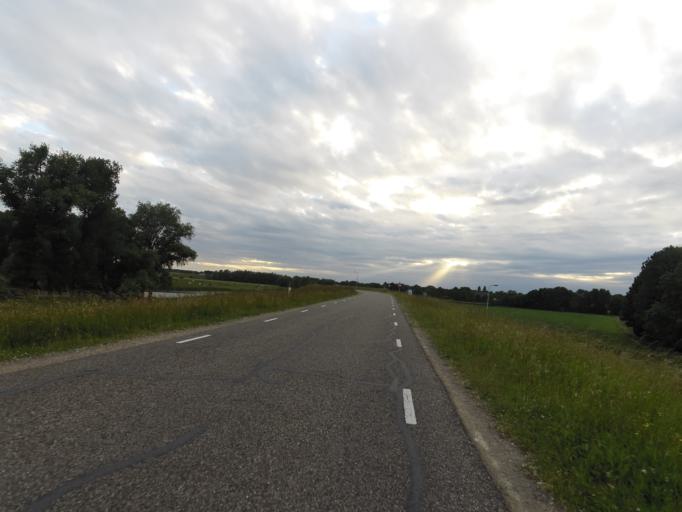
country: NL
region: Gelderland
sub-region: Gemeente Duiven
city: Duiven
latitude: 51.8759
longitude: 5.9850
